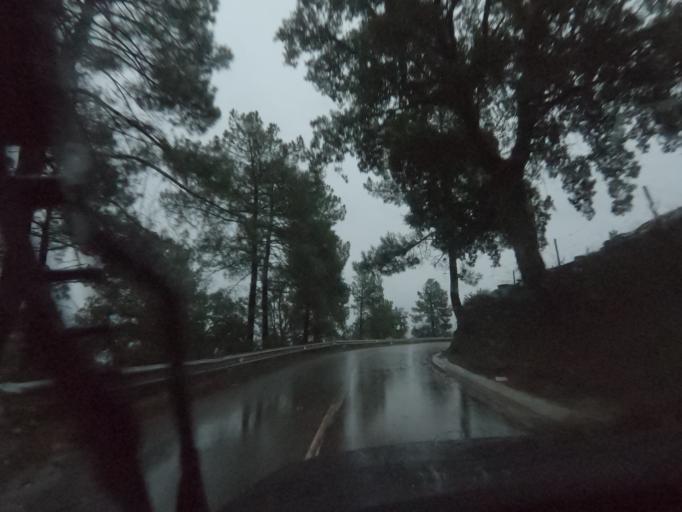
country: PT
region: Vila Real
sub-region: Sabrosa
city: Sabrosa
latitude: 41.2261
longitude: -7.5557
